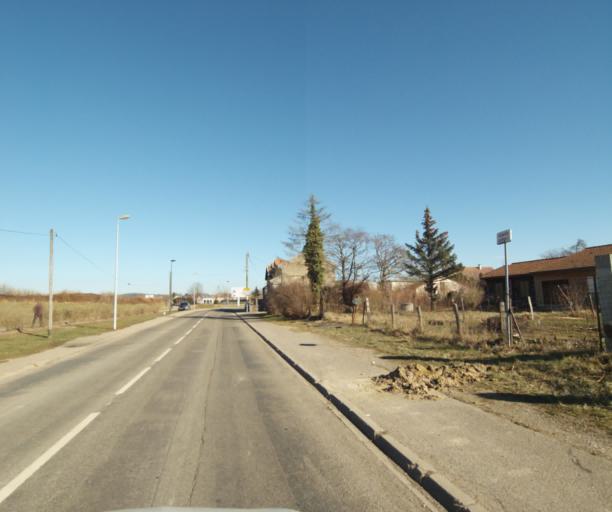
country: FR
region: Lorraine
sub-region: Departement de Meurthe-et-Moselle
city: Tomblaine
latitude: 48.6845
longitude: 6.2260
